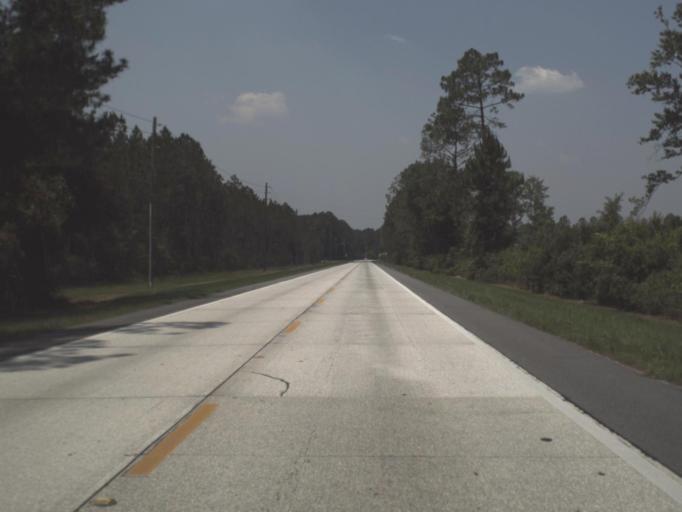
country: US
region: Florida
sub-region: Duval County
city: Baldwin
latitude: 30.2031
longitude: -81.9980
